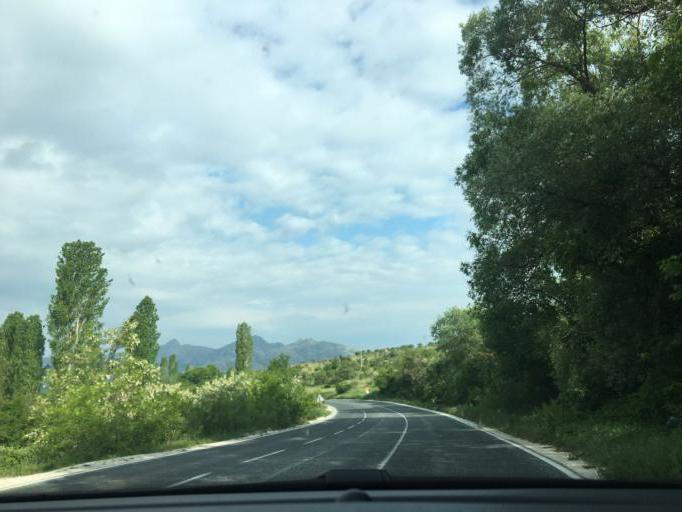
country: MK
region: Prilep
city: Prilep
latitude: 41.3677
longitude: 21.6421
